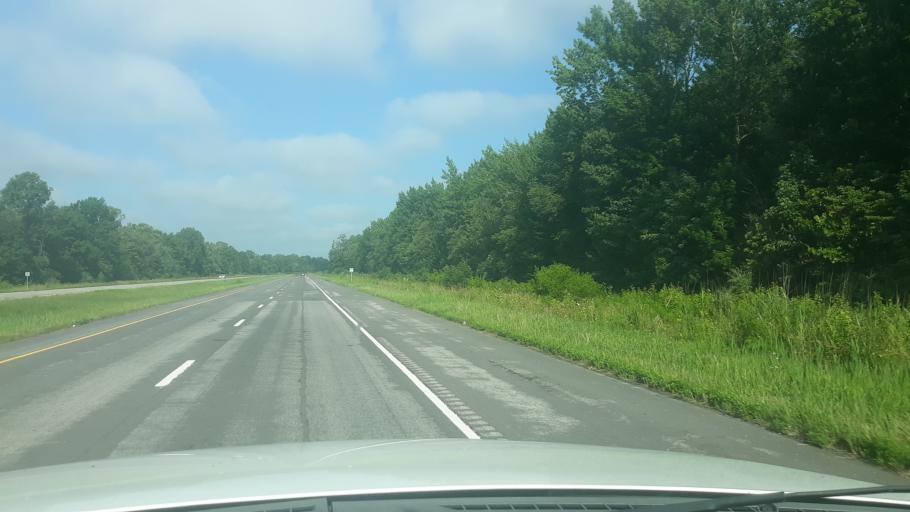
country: US
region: Illinois
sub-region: Saline County
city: Carrier Mills
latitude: 37.7344
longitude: -88.6884
